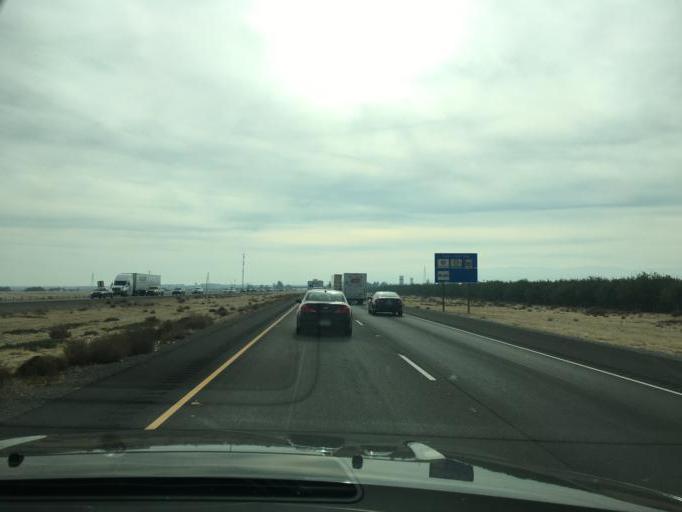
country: US
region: California
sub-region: Fresno County
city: Mendota
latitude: 36.6479
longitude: -120.6294
